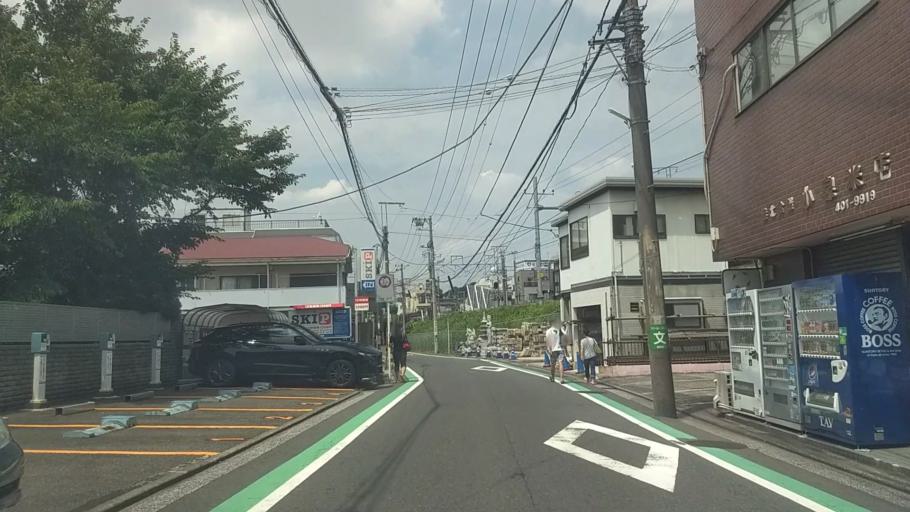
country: JP
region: Kanagawa
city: Yokohama
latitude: 35.5084
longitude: 139.6342
